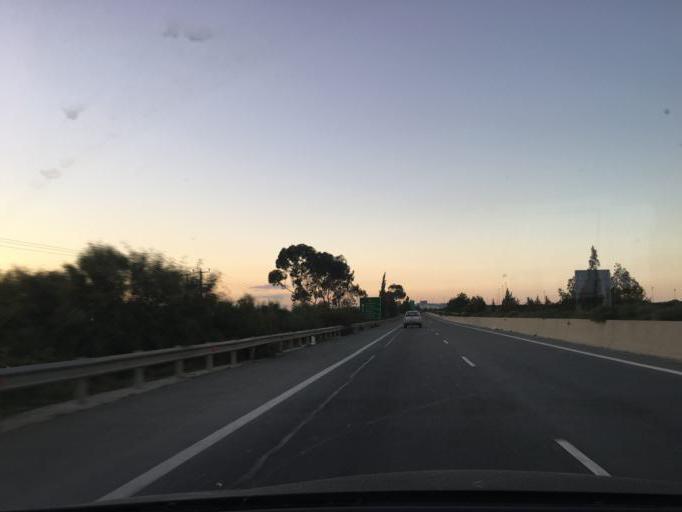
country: CY
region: Larnaka
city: Dhromolaxia
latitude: 34.8933
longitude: 33.5805
